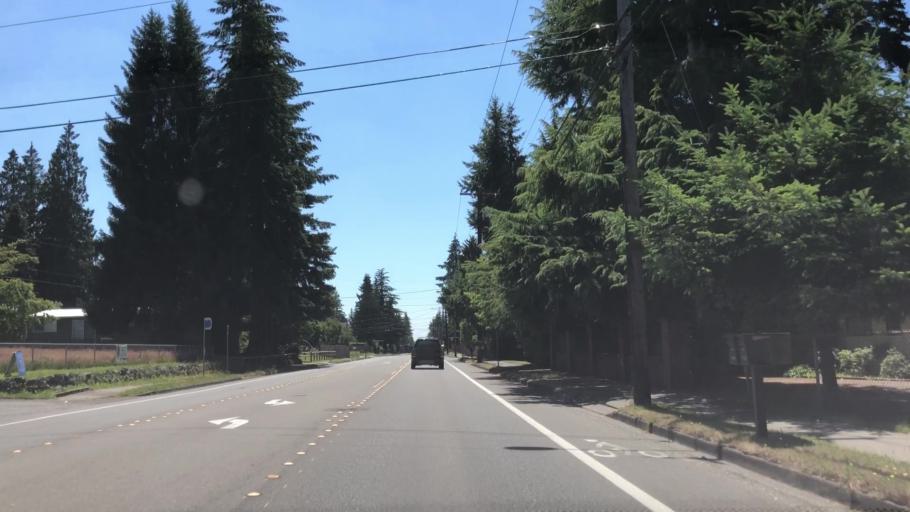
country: US
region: Washington
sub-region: Snohomish County
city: Alderwood Manor
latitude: 47.8375
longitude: -122.2925
